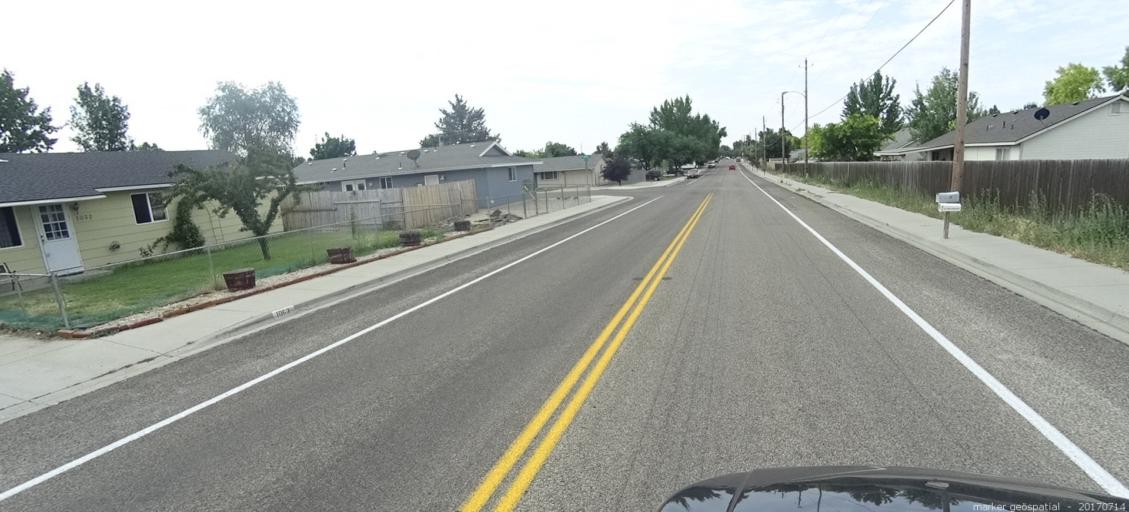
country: US
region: Idaho
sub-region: Ada County
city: Kuna
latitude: 43.4987
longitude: -116.4237
